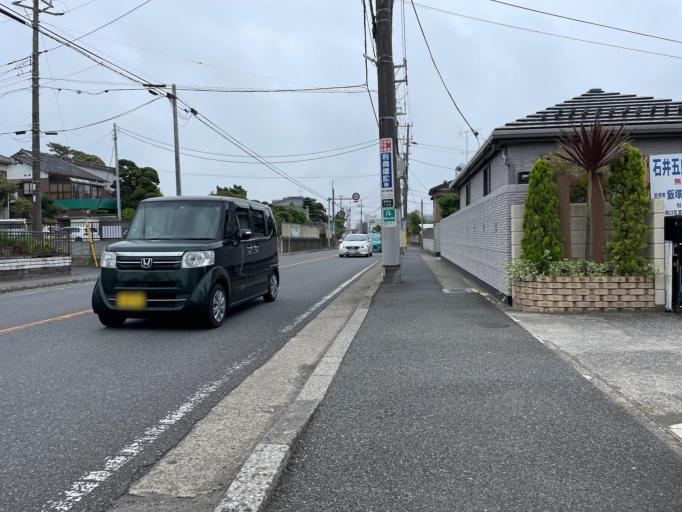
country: JP
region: Chiba
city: Funabashi
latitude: 35.7142
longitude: 139.9485
